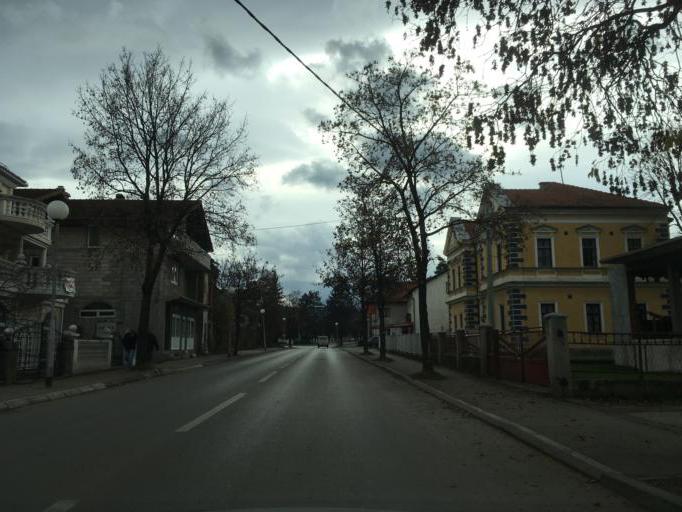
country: BA
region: Federation of Bosnia and Herzegovina
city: Bugojno
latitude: 44.0586
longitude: 17.4496
